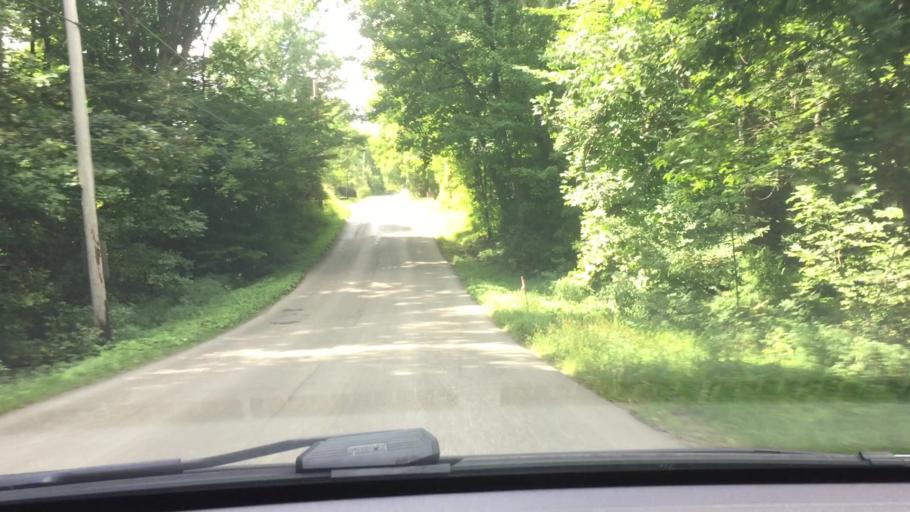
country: US
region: Pennsylvania
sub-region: Lawrence County
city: New Wilmington
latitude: 41.1151
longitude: -80.3443
